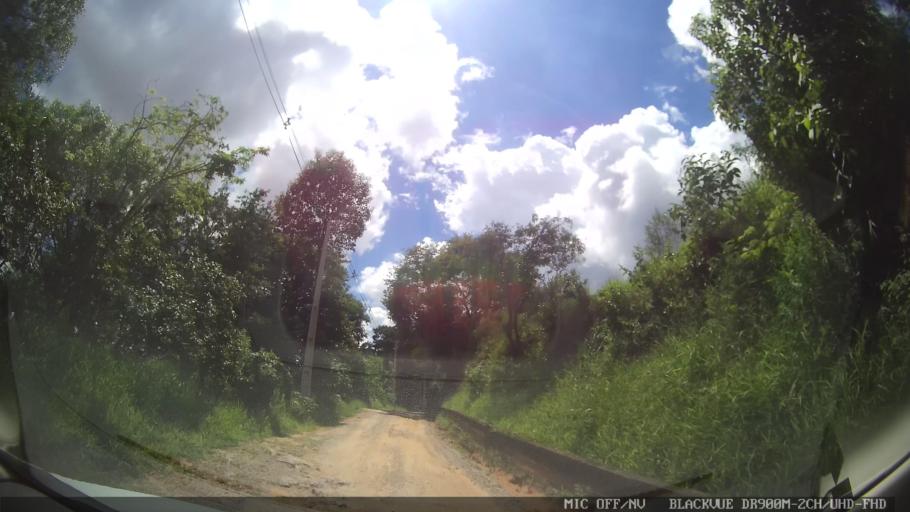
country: BR
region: Minas Gerais
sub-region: Extrema
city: Extrema
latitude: -22.8708
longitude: -46.3250
